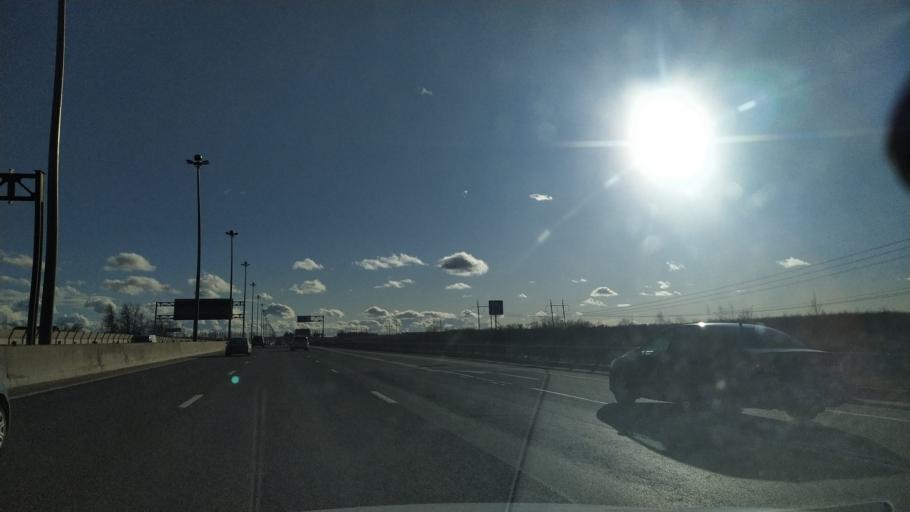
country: RU
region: St.-Petersburg
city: Aleksandrovskaya
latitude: 59.7428
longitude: 30.3078
